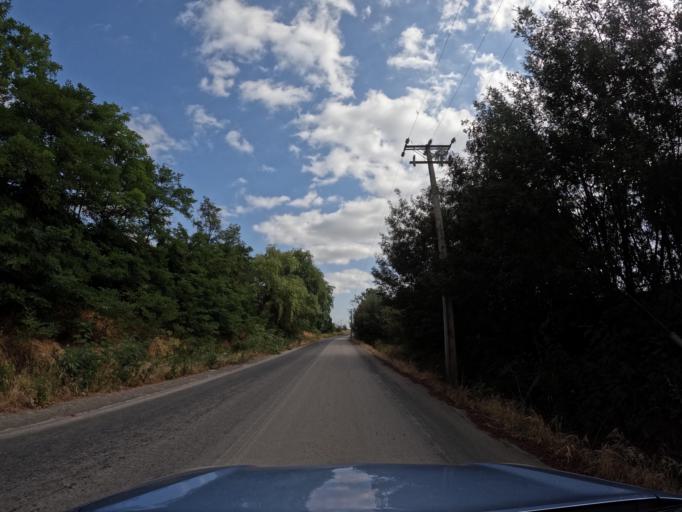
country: CL
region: Maule
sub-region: Provincia de Curico
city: Molina
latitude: -35.1697
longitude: -71.2920
